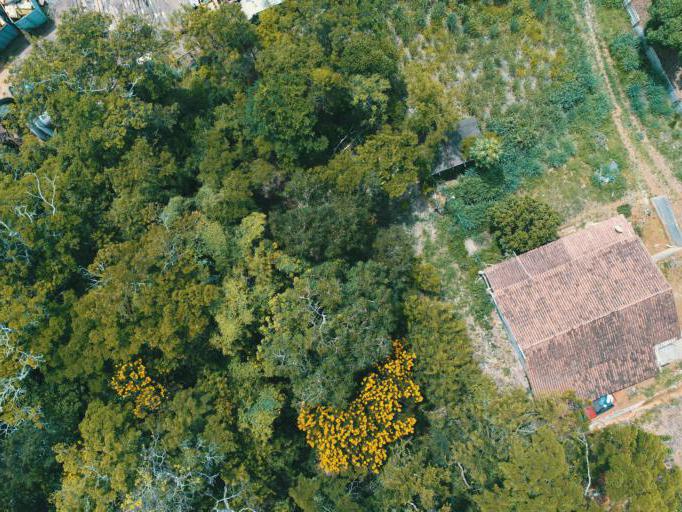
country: BR
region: Rio de Janeiro
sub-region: Macae
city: Macae
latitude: -22.4390
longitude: -41.8694
